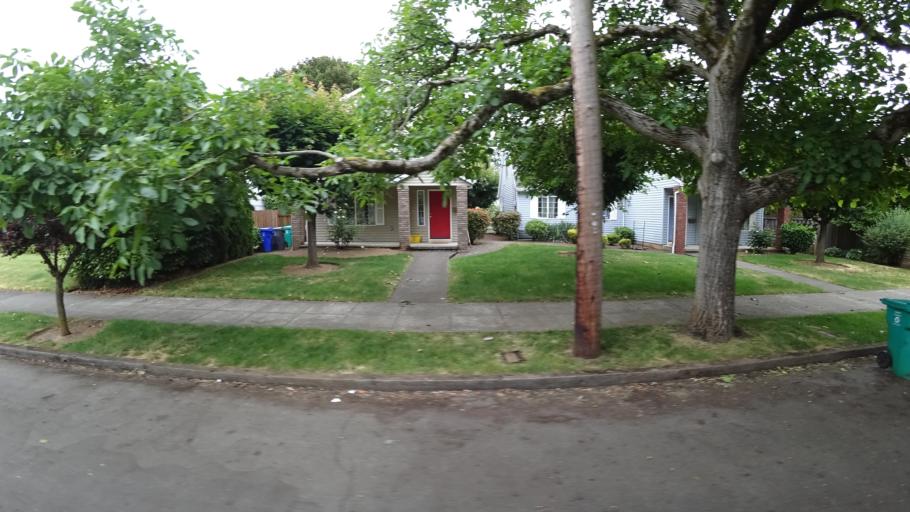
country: US
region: Oregon
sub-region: Washington County
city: West Haven
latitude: 45.5787
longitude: -122.7311
